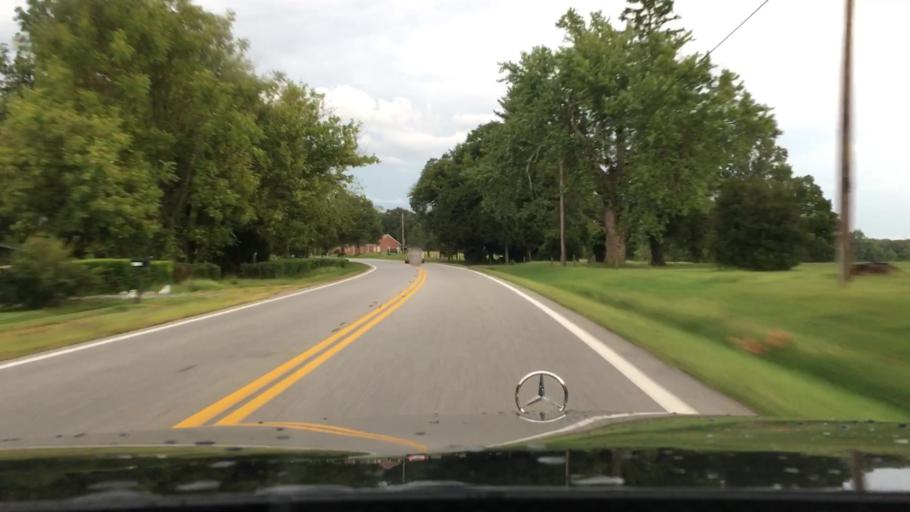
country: US
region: Virginia
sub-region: Amherst County
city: Amherst
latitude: 37.6381
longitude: -79.0226
